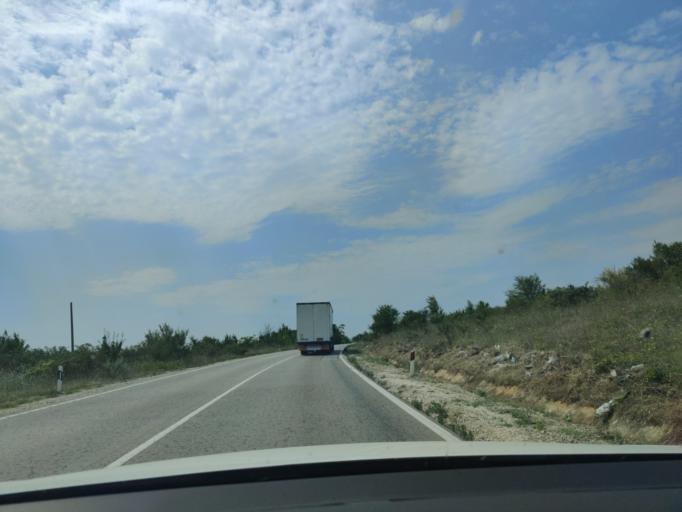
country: BG
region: Vidin
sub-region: Obshtina Vidin
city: Dunavtsi
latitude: 43.8815
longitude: 22.7924
